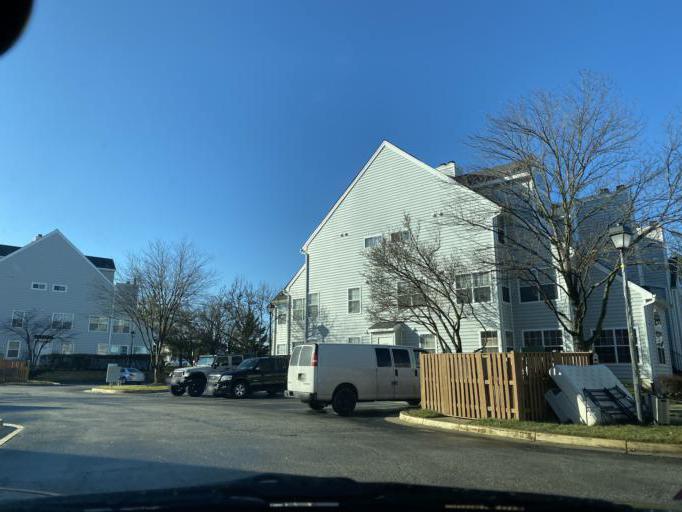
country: US
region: Maryland
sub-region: Prince George's County
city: South Laurel
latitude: 39.0855
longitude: -76.8683
